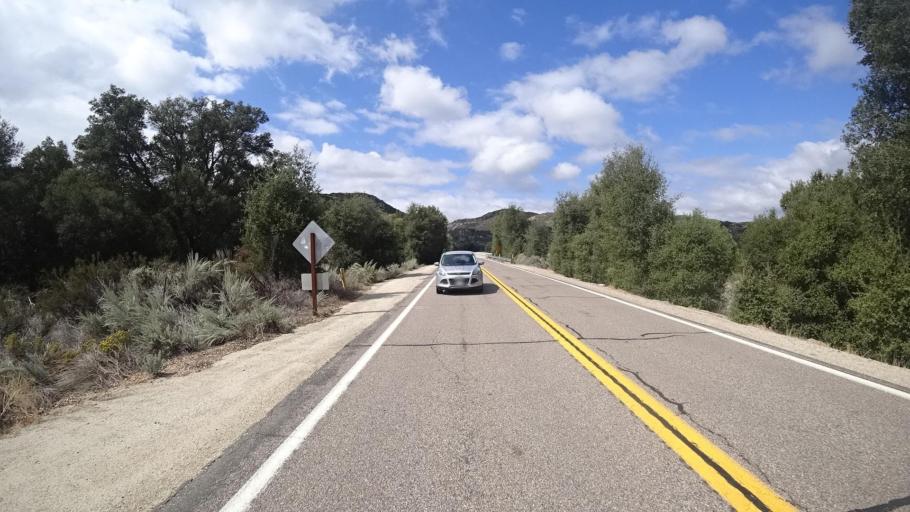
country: US
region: California
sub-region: San Diego County
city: Campo
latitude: 32.7142
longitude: -116.4977
